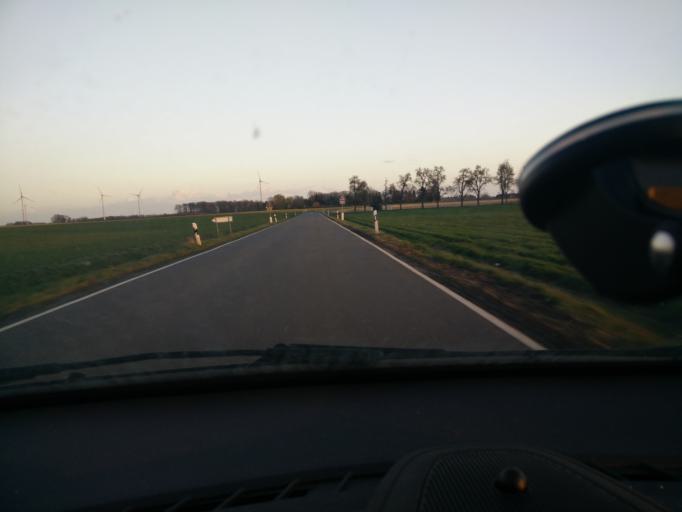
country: DE
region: North Rhine-Westphalia
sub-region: Regierungsbezirk Munster
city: Raesfeld
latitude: 51.7951
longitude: 6.8927
